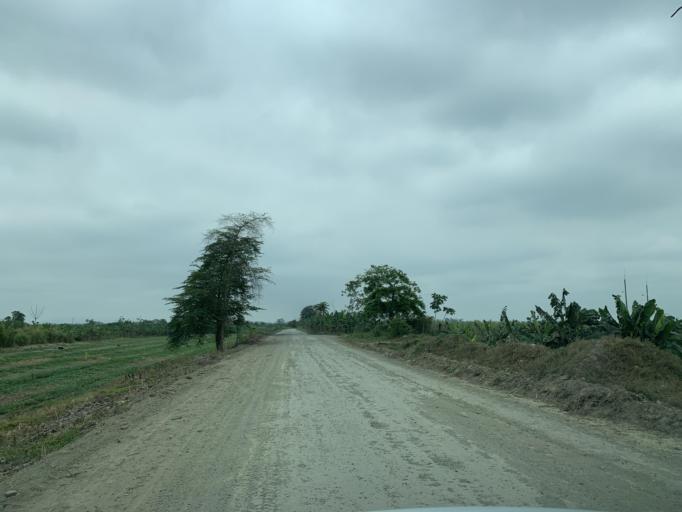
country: EC
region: Canar
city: La Troncal
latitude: -2.3696
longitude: -79.4421
